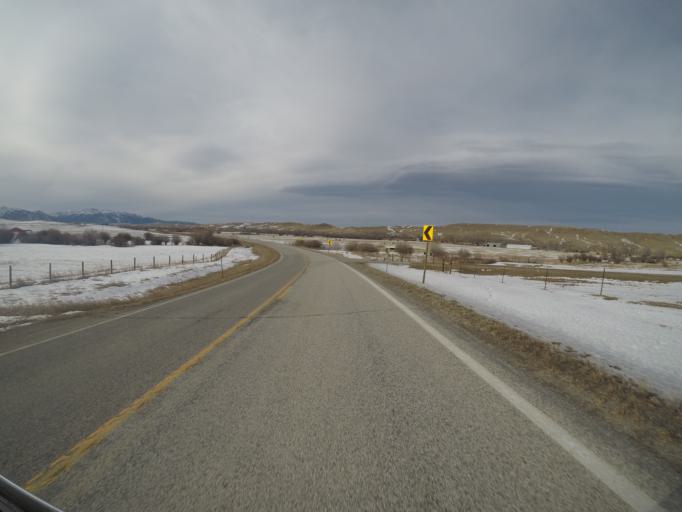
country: US
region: Montana
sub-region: Carbon County
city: Red Lodge
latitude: 45.3051
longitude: -109.3643
